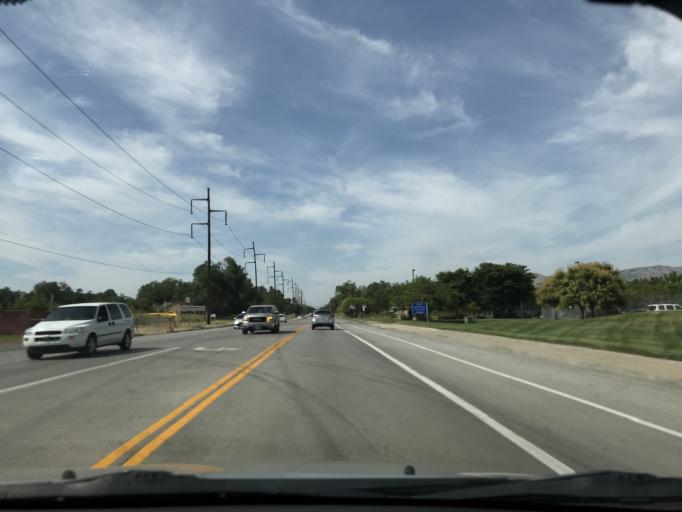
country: US
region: Utah
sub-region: Salt Lake County
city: South Salt Lake
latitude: 40.7337
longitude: -111.9168
